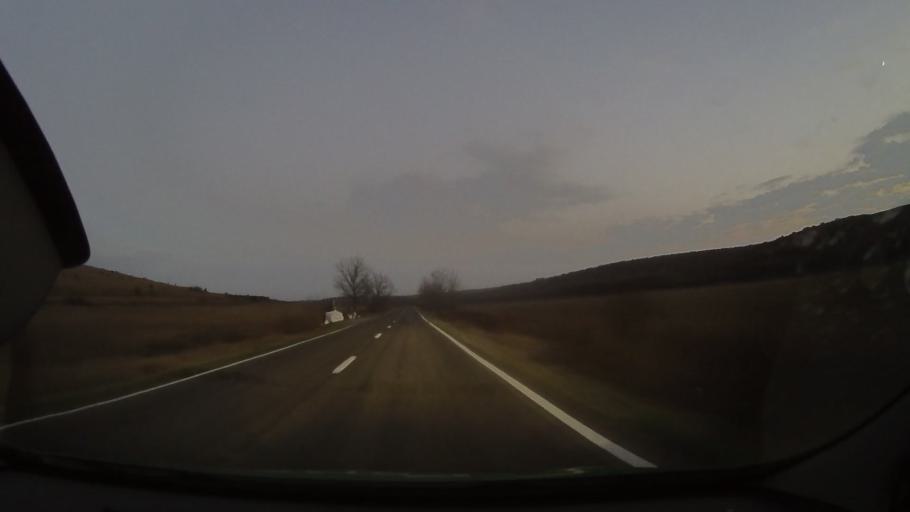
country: RO
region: Constanta
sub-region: Comuna Ion Corvin
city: Ion Corvin
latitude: 44.1076
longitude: 27.7784
